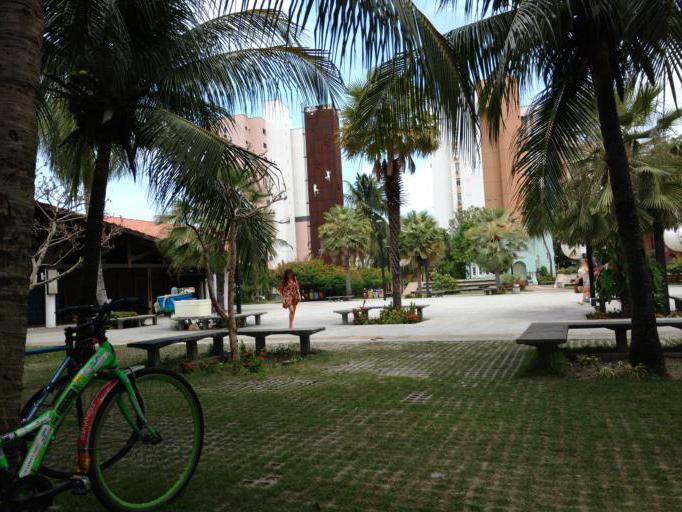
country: BR
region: Ceara
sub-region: Fortaleza
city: Fortaleza
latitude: -3.7319
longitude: -38.5100
